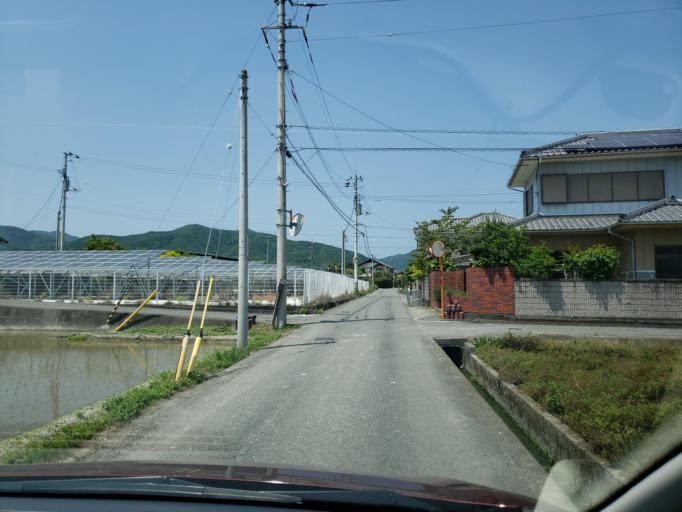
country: JP
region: Tokushima
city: Kamojimacho-jogejima
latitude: 34.0859
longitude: 134.2681
